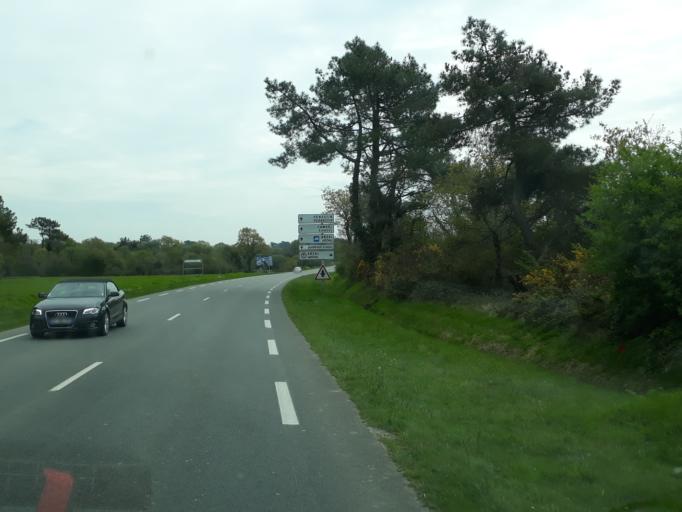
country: FR
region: Brittany
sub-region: Departement du Morbihan
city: Peaule
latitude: 47.5269
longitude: -2.3822
